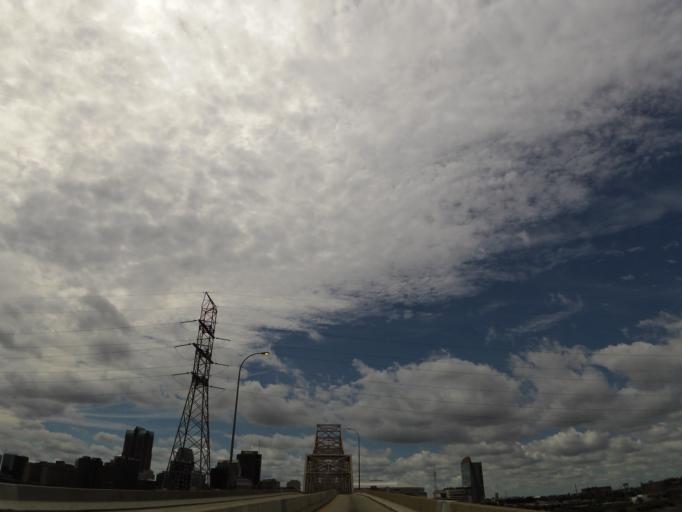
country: US
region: Missouri
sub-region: City of Saint Louis
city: St. Louis
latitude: 38.6307
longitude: -90.1743
